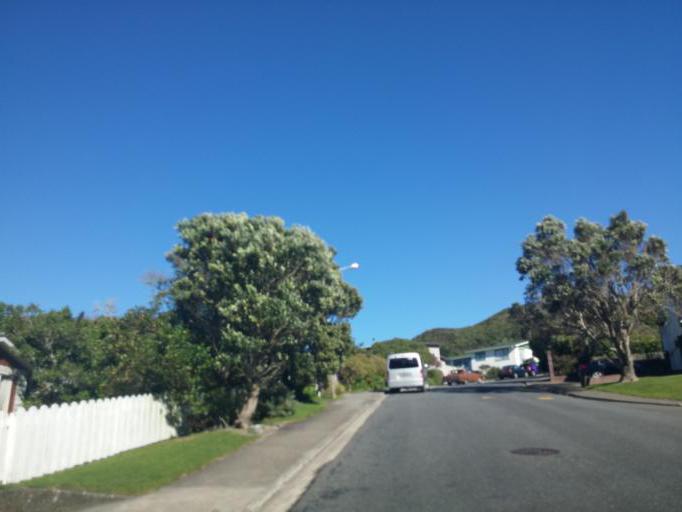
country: NZ
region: Wellington
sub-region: Wellington City
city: Wellington
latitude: -41.2215
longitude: 174.7965
